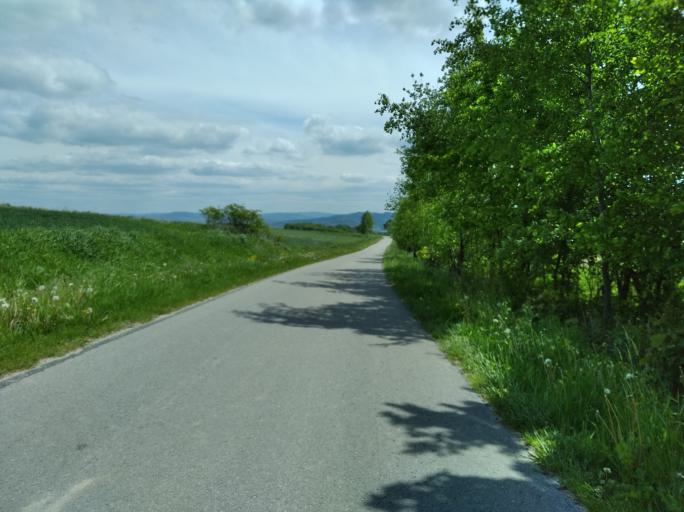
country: PL
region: Subcarpathian Voivodeship
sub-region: Powiat ropczycko-sedziszowski
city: Wielopole Skrzynskie
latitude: 49.9002
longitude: 21.6089
